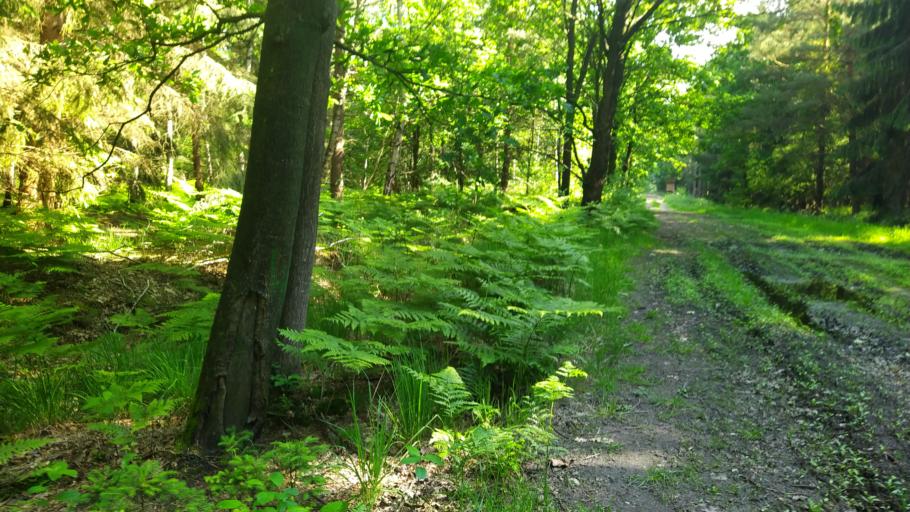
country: DE
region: Lower Saxony
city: Wohnste
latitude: 53.3945
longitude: 9.5151
